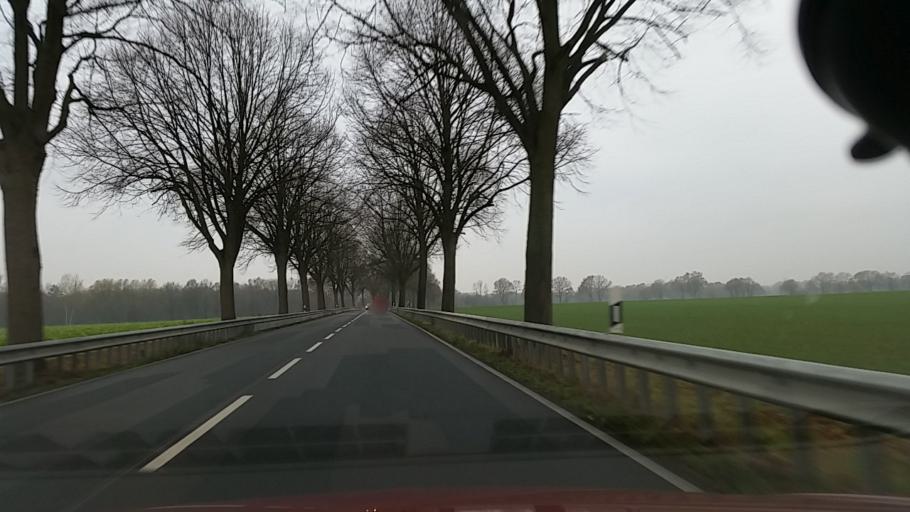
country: DE
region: Lower Saxony
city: Hankensbuttel
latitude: 52.7320
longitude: 10.6307
